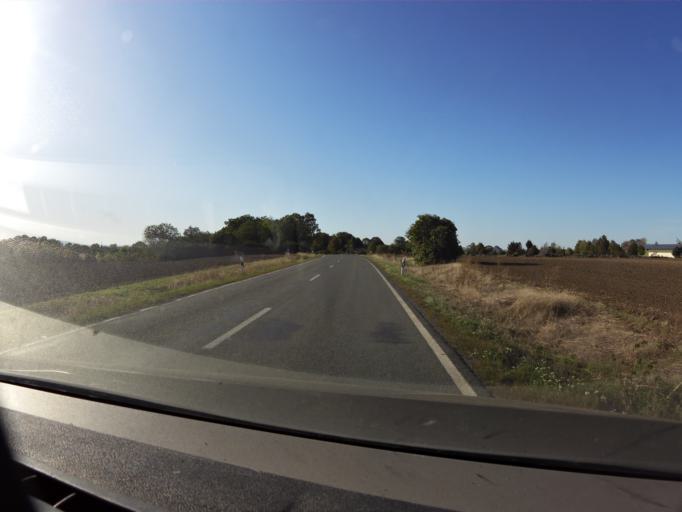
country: DE
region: Saxony-Anhalt
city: Hedersleben
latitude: 51.8767
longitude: 11.2255
